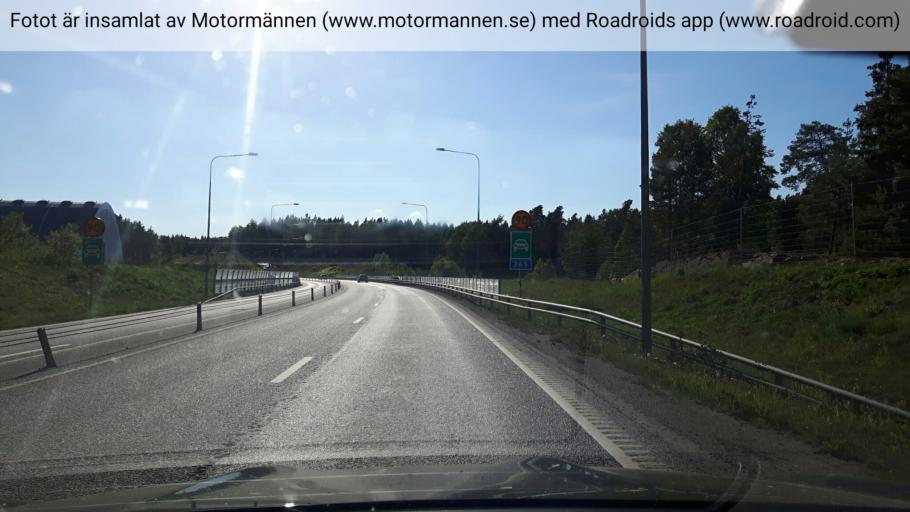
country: SE
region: Stockholm
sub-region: Vallentuna Kommun
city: Vallentuna
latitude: 59.4981
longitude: 18.1603
